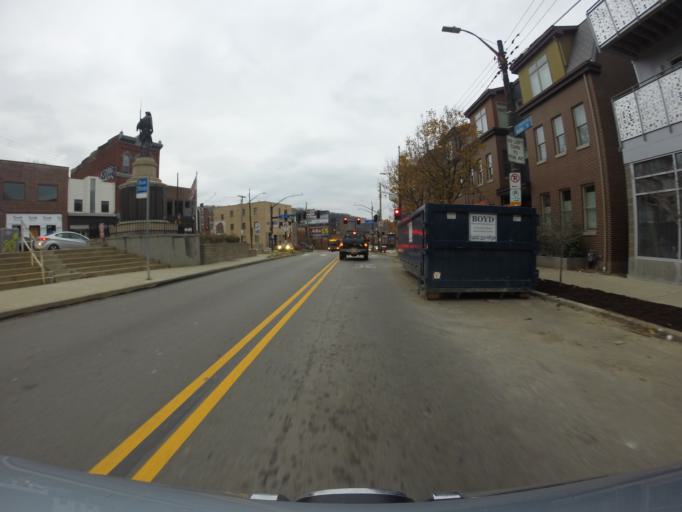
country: US
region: Pennsylvania
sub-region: Allegheny County
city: Bloomfield
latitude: 40.4632
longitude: -79.9669
